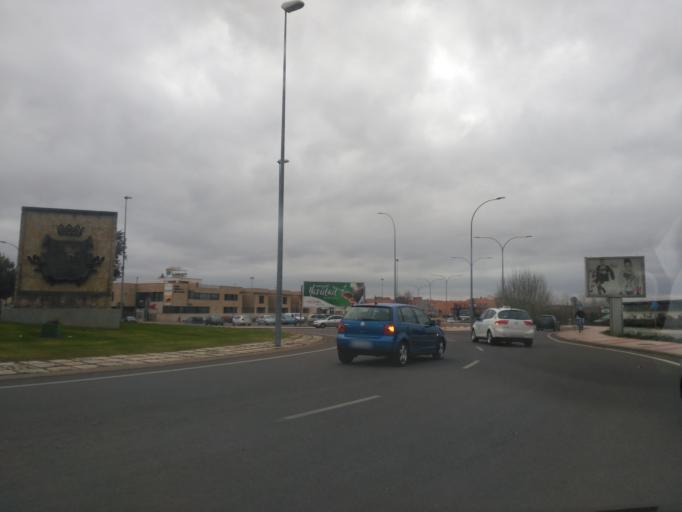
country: ES
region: Castille and Leon
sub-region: Provincia de Salamanca
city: Salamanca
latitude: 40.9582
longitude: -5.6752
